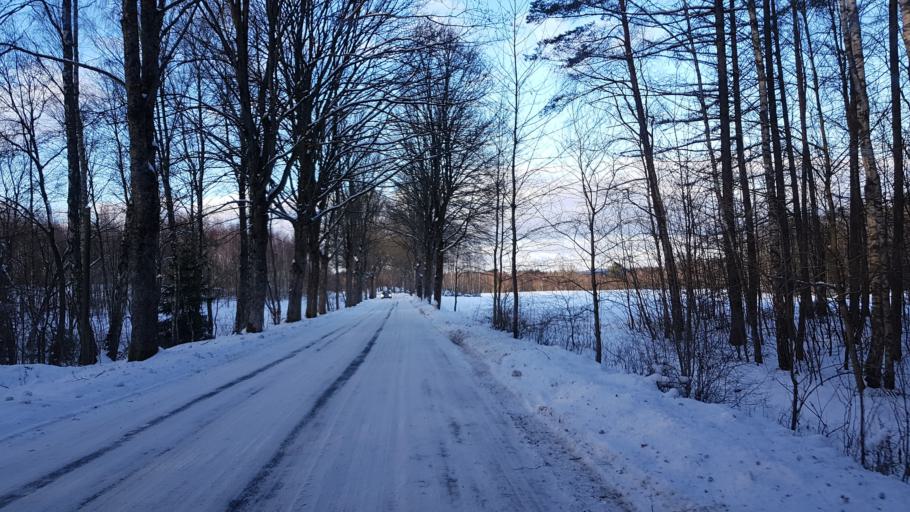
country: PL
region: West Pomeranian Voivodeship
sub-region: Powiat koszalinski
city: Bobolice
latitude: 53.9708
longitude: 16.7009
